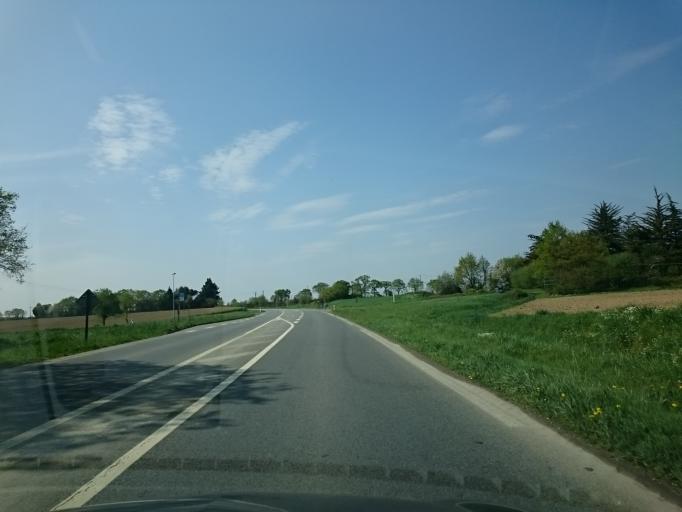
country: FR
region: Brittany
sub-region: Departement d'Ille-et-Vilaine
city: Vern-sur-Seiche
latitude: 48.0736
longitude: -1.5770
